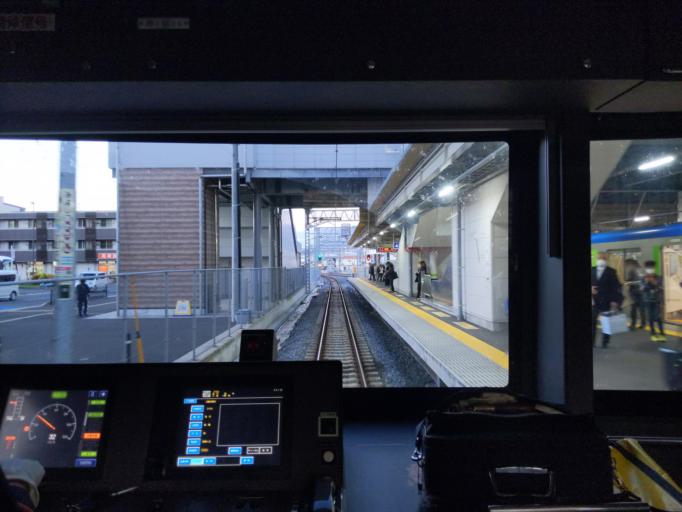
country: JP
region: Chiba
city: Kashiwa
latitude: 35.8082
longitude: 139.9987
